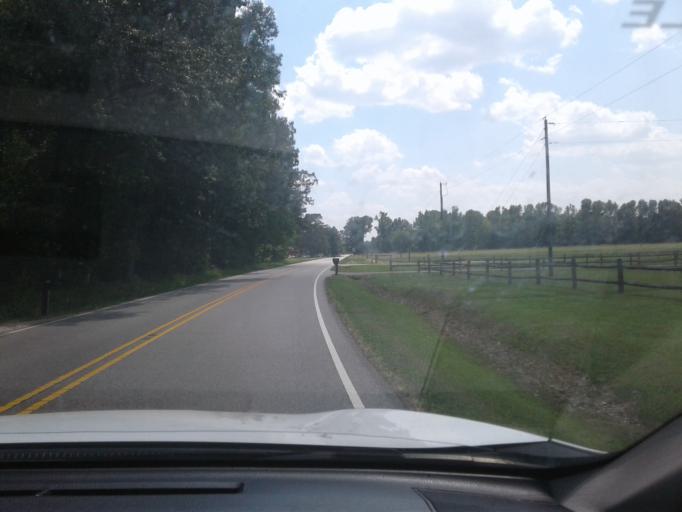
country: US
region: North Carolina
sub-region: Harnett County
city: Erwin
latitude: 35.2280
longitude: -78.6813
